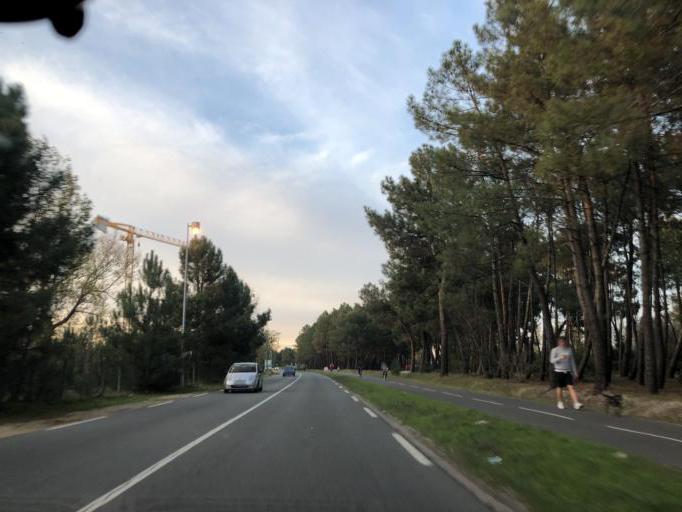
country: FR
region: Aquitaine
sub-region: Departement de la Gironde
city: Le Bouscat
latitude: 44.8820
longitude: -0.5843
